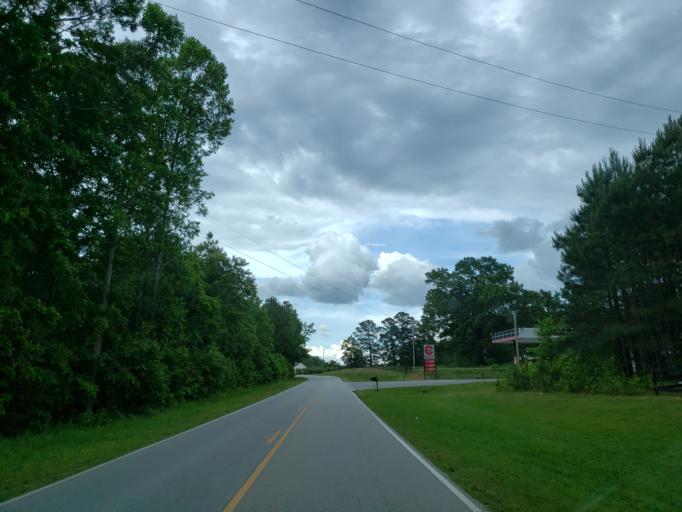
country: US
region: Georgia
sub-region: Polk County
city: Rockmart
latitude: 33.9029
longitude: -85.0711
